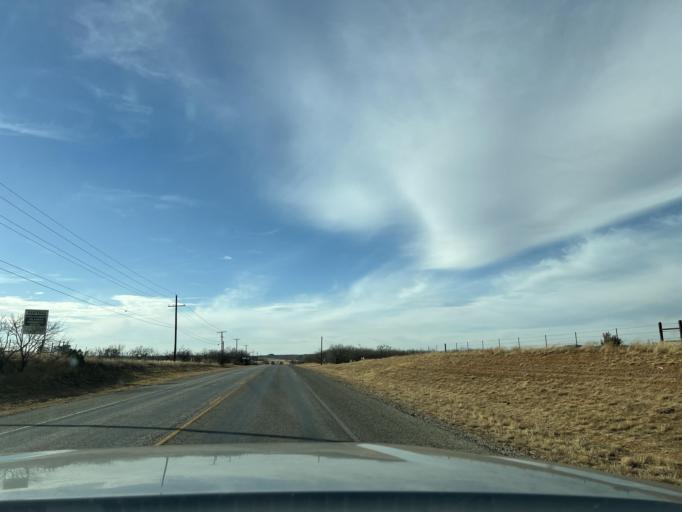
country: US
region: Texas
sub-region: Fisher County
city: Rotan
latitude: 32.7327
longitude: -100.6558
